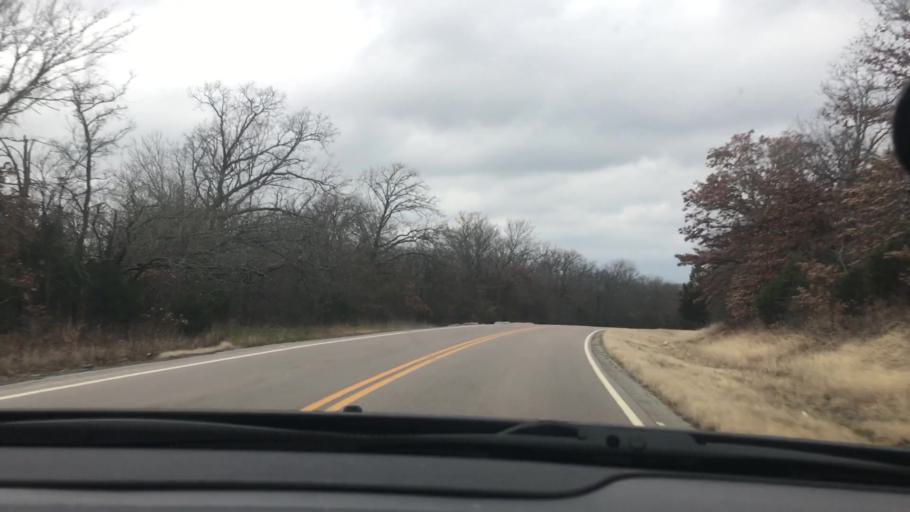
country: US
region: Oklahoma
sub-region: Coal County
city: Coalgate
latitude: 34.3699
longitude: -96.3836
